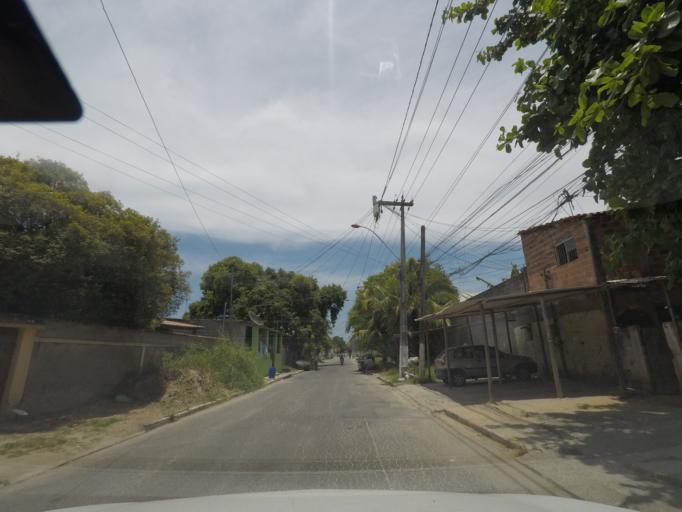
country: BR
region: Rio de Janeiro
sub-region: Marica
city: Marica
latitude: -22.9094
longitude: -42.8370
